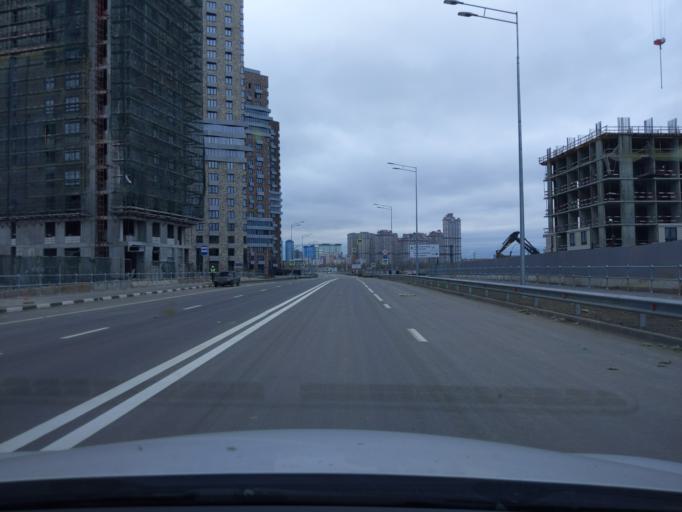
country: RU
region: Moscow
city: Strogino
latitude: 55.8164
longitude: 37.4266
